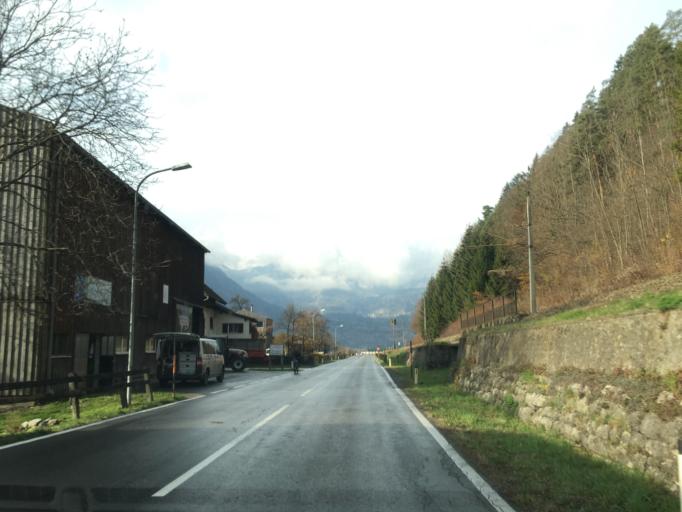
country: AT
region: Vorarlberg
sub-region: Politischer Bezirk Bludenz
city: Stallehr
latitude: 47.1448
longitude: 9.8490
